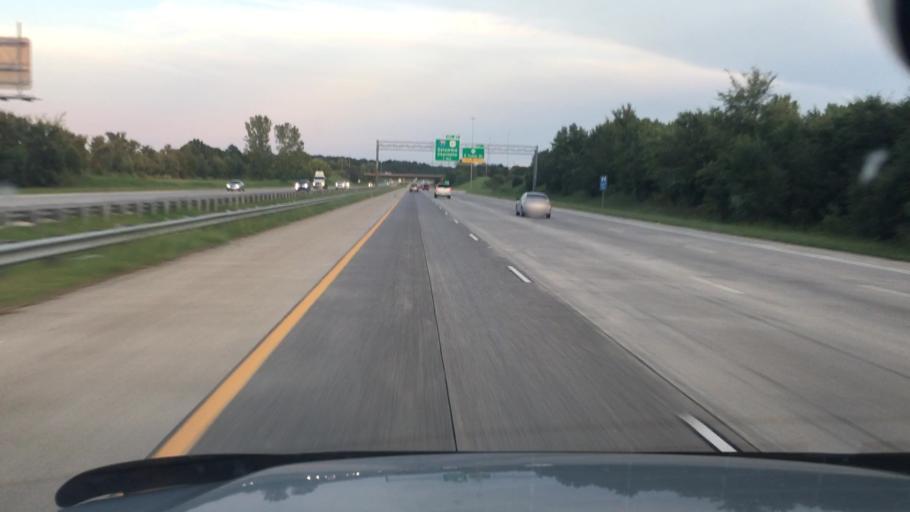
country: US
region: North Carolina
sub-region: Mecklenburg County
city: Pineville
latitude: 35.1460
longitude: -80.9388
